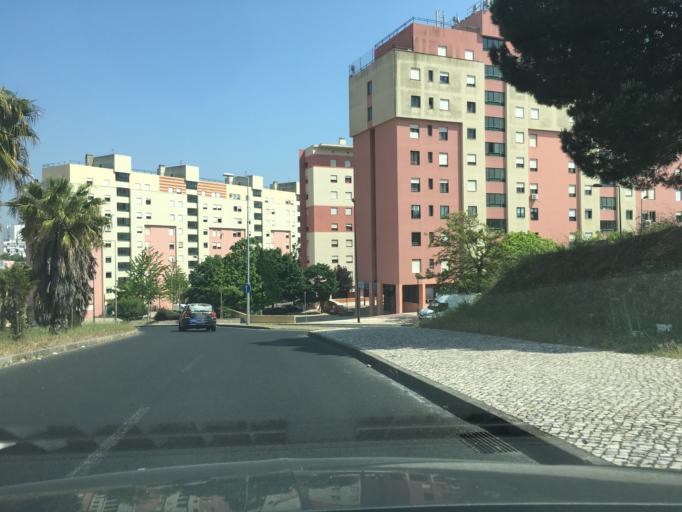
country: PT
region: Lisbon
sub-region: Lisbon
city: Lisbon
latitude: 38.7476
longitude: -9.1203
